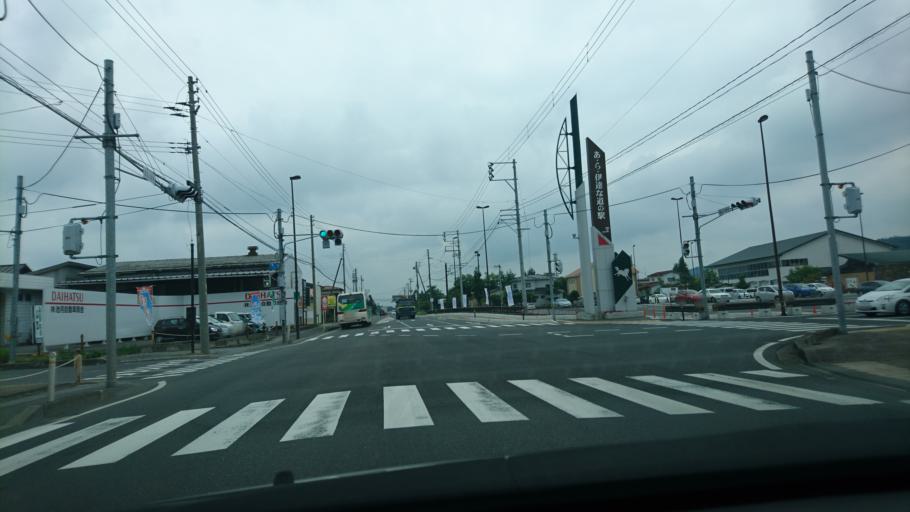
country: JP
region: Miyagi
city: Furukawa
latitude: 38.7084
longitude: 140.8339
